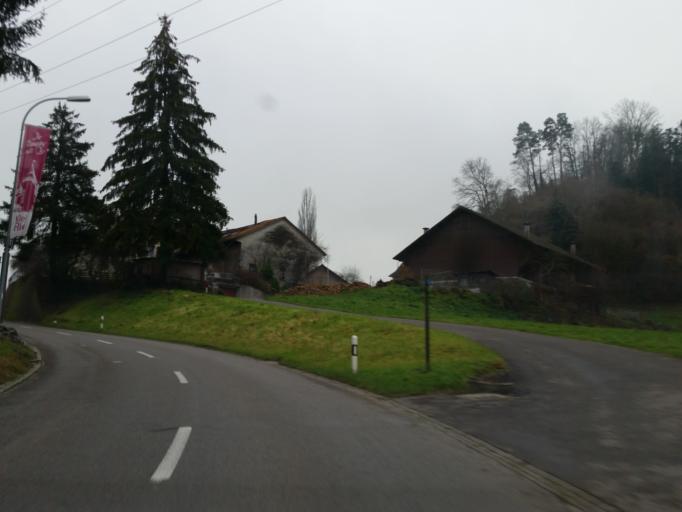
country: CH
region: Thurgau
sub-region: Weinfelden District
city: Sulgen
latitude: 47.5184
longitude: 9.1971
